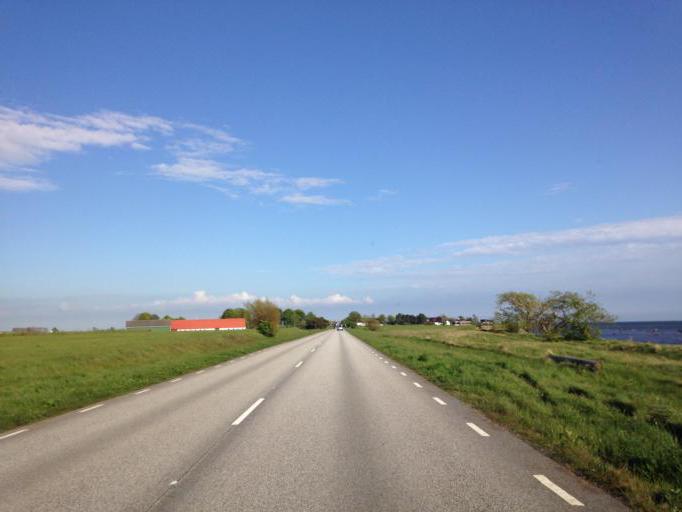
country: SE
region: Skane
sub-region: Trelleborgs Kommun
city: Skare
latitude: 55.3801
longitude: 13.0396
